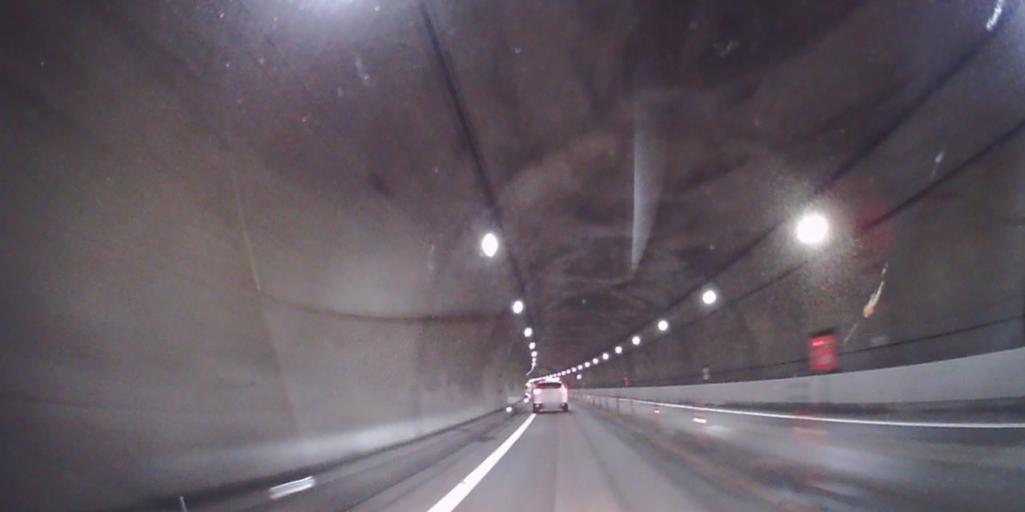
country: JP
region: Hokkaido
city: Date
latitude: 42.5897
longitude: 140.7193
